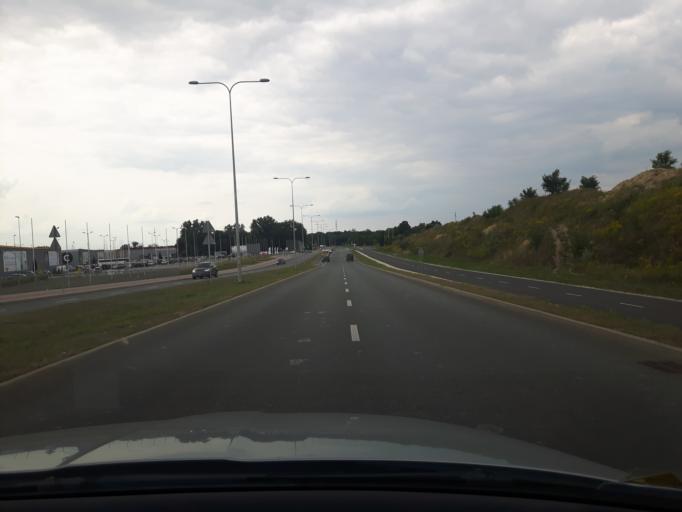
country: PL
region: Masovian Voivodeship
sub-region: Powiat pruszkowski
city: Nadarzyn
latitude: 52.1082
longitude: 20.8356
